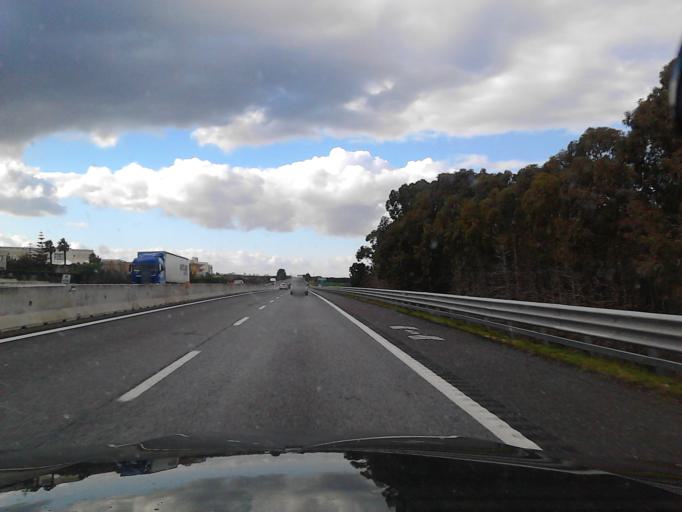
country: IT
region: Apulia
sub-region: Provincia di Barletta - Andria - Trani
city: Andria
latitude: 41.2498
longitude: 16.3314
